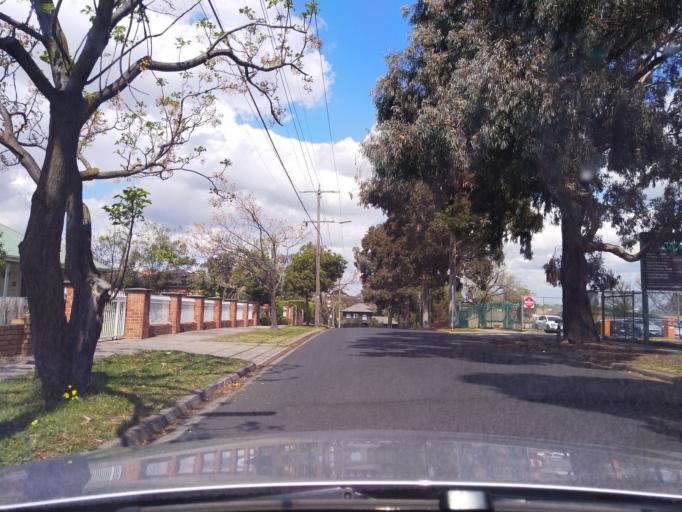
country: AU
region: Victoria
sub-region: Banyule
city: Bellfield
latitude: -37.7564
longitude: 145.0497
